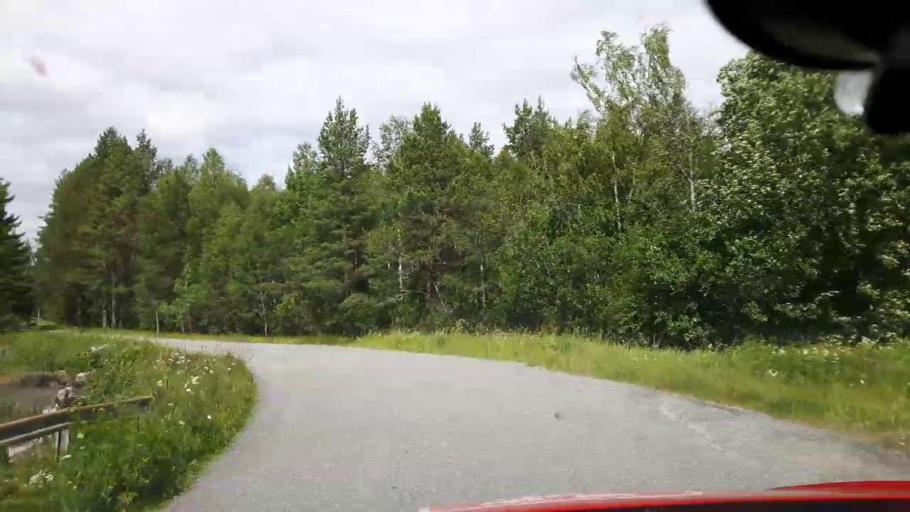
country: SE
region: Jaemtland
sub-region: Braecke Kommun
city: Braecke
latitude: 62.8483
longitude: 15.2981
